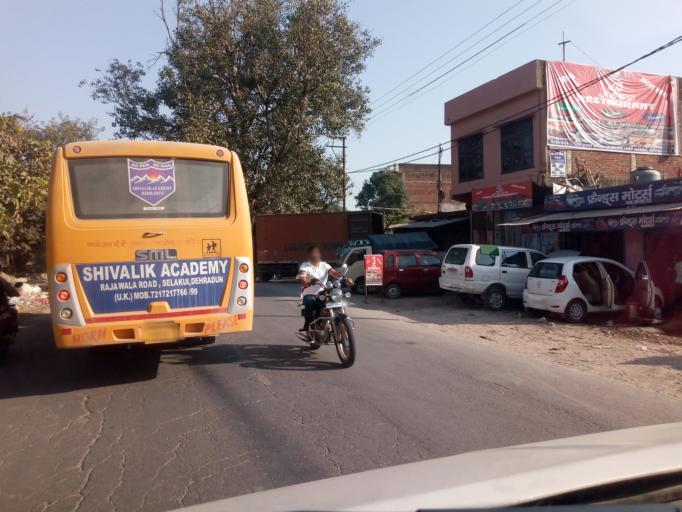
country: IN
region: Uttarakhand
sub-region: Dehradun
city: Vikasnagar
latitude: 30.3531
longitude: 77.8596
